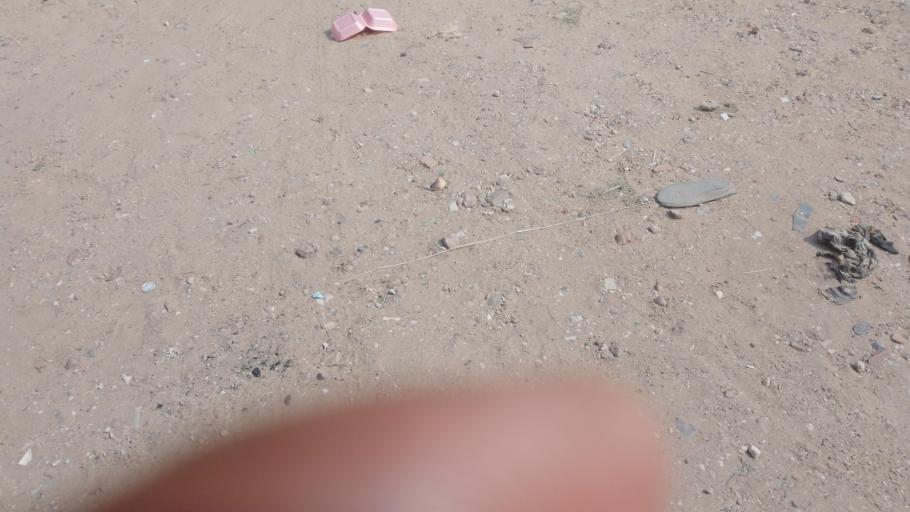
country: ZM
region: Lusaka
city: Lusaka
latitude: -15.4082
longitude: 28.3733
